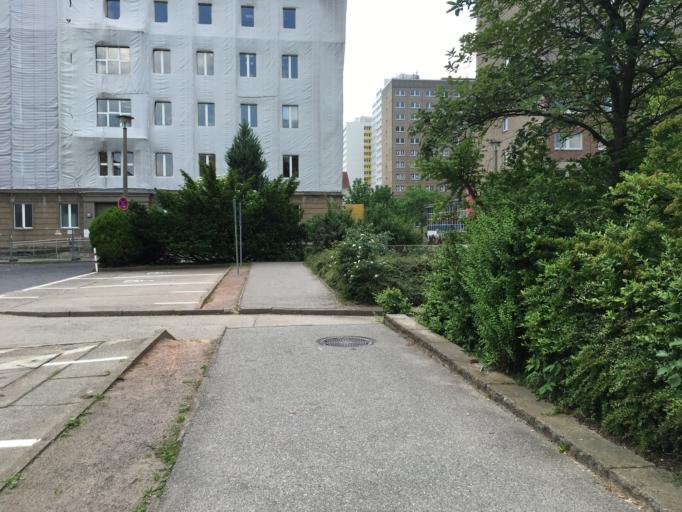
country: DE
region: Berlin
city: Lichtenberg
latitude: 52.5142
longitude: 13.4866
